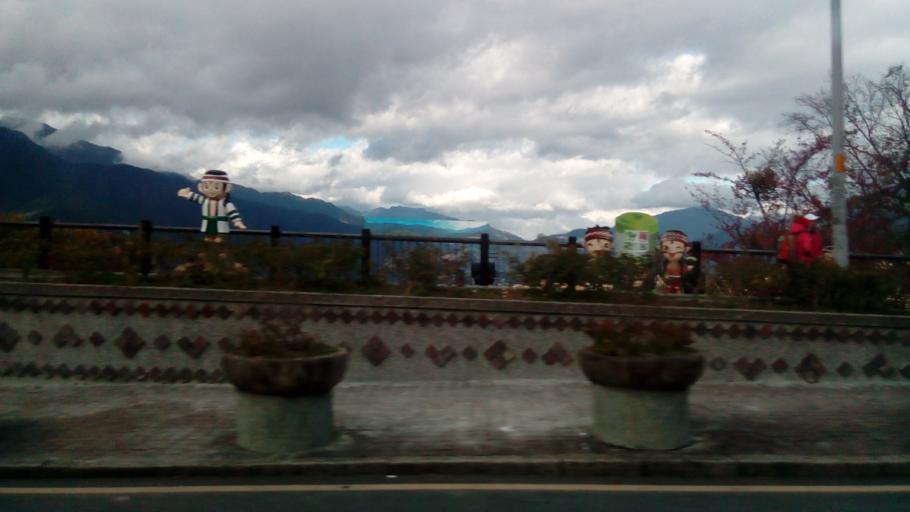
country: TW
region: Taiwan
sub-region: Nantou
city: Puli
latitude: 24.2547
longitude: 121.2514
